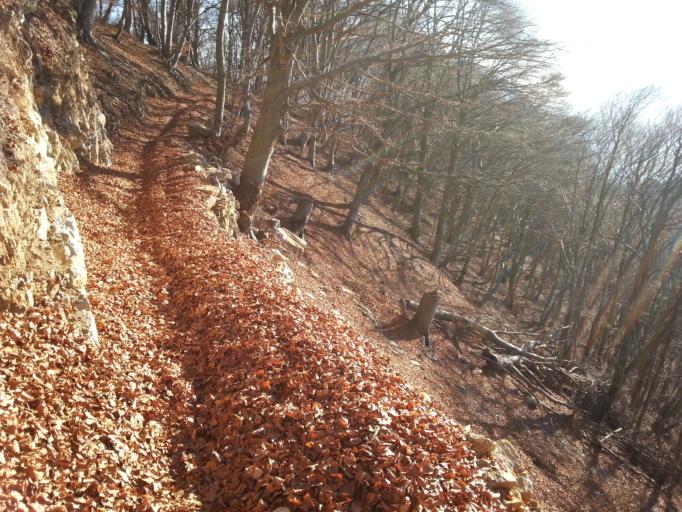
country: CH
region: Ticino
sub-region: Lugano District
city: Pregassona
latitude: 46.0208
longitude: 8.9927
